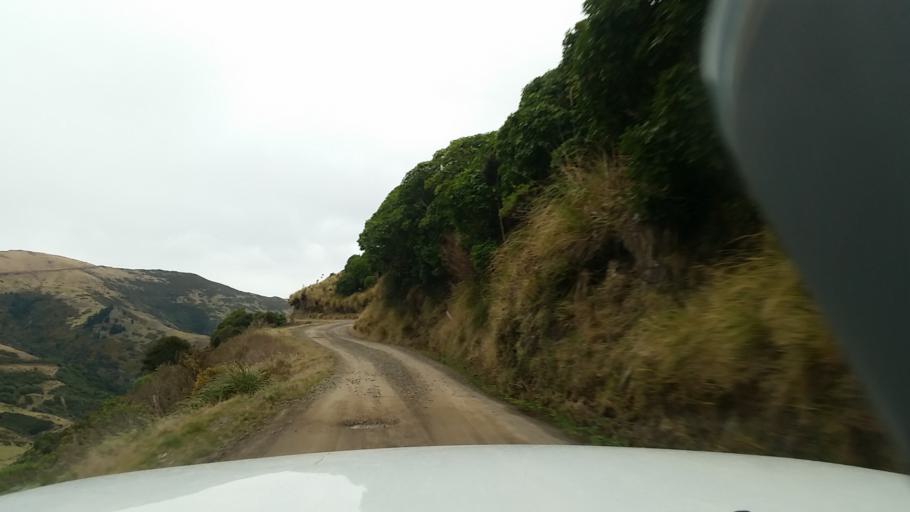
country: NZ
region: Canterbury
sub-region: Christchurch City
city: Christchurch
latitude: -43.8080
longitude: 172.8565
